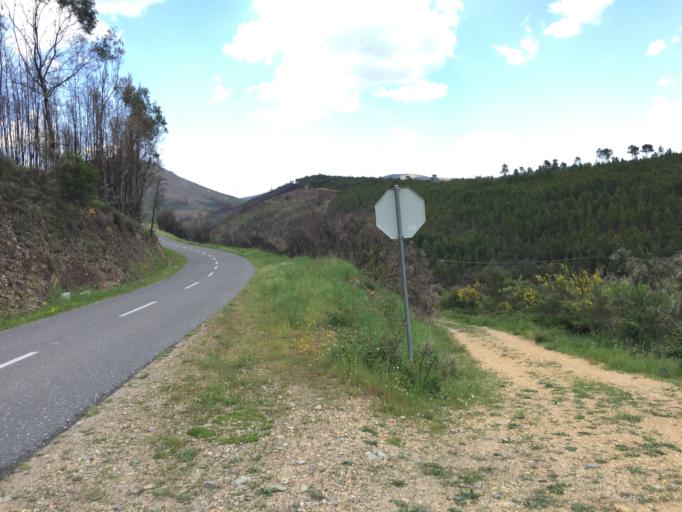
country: PT
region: Coimbra
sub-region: Pampilhosa da Serra
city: Pampilhosa da Serra
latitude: 40.0987
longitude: -7.8641
